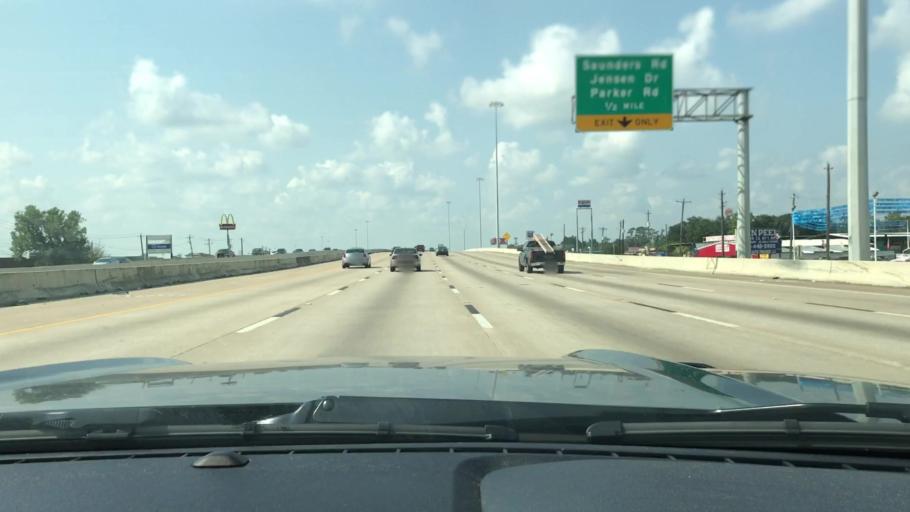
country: US
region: Texas
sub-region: Harris County
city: Aldine
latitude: 29.8734
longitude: -95.3285
